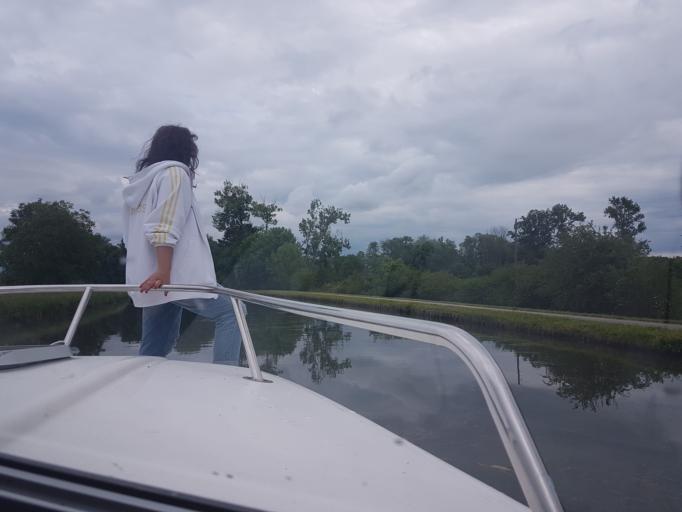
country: FR
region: Bourgogne
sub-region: Departement de l'Yonne
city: Saint-Bris-le-Vineux
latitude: 47.6972
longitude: 3.6427
